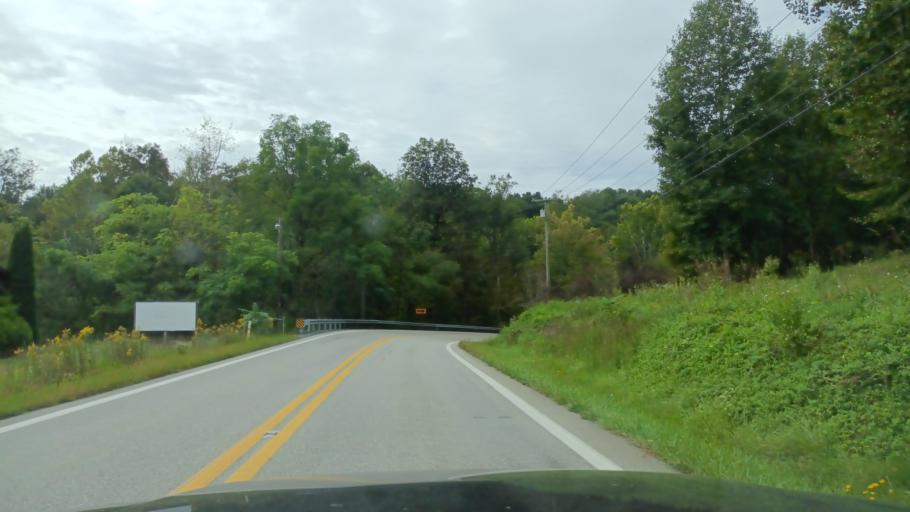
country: US
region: West Virginia
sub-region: Taylor County
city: Grafton
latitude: 39.3281
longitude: -80.0994
